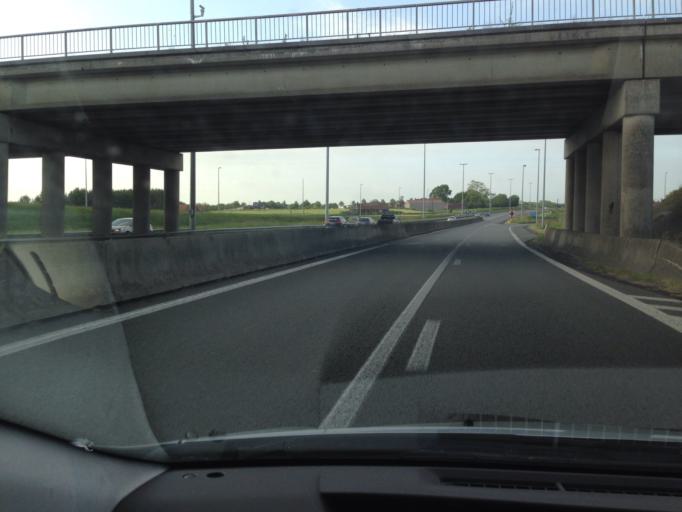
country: BE
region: Flanders
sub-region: Provincie West-Vlaanderen
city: Lichtervelde
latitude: 51.0783
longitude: 3.1536
